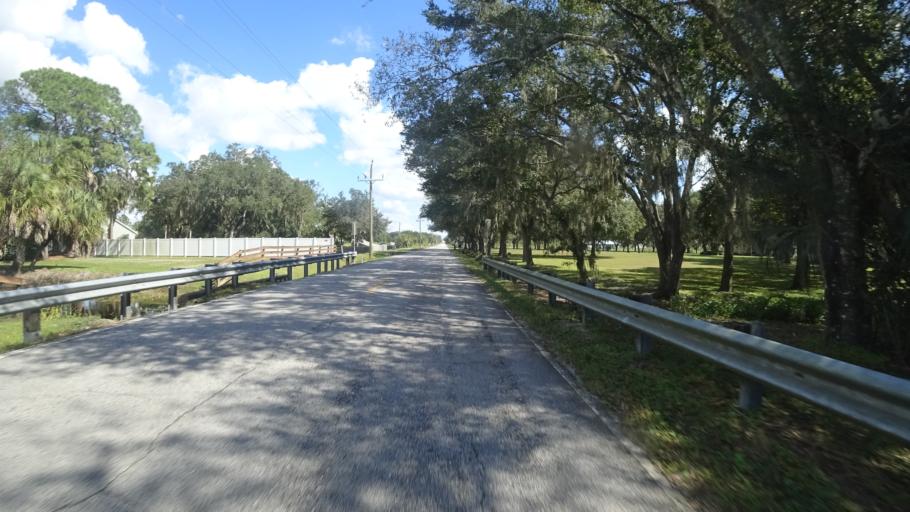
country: US
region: Florida
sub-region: Manatee County
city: Ellenton
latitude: 27.4878
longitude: -82.3815
